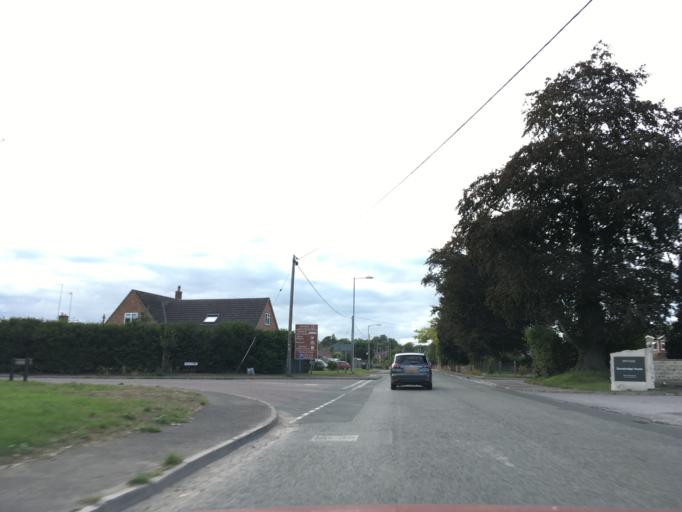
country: GB
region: England
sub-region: Wiltshire
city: Devizes
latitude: 51.3443
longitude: -1.9783
